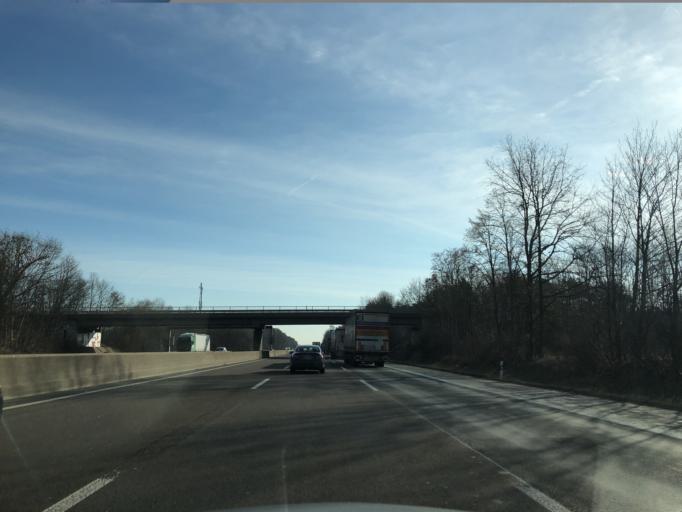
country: DE
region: Hesse
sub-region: Regierungsbezirk Darmstadt
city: Seligenstadt
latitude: 50.0057
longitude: 8.9853
